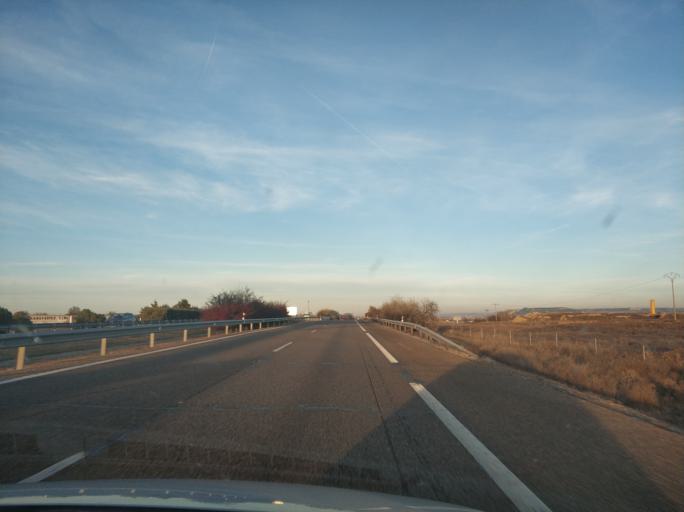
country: ES
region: Castille and Leon
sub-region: Provincia de Valladolid
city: Santovenia de Pisuerga
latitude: 41.6943
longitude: -4.7220
